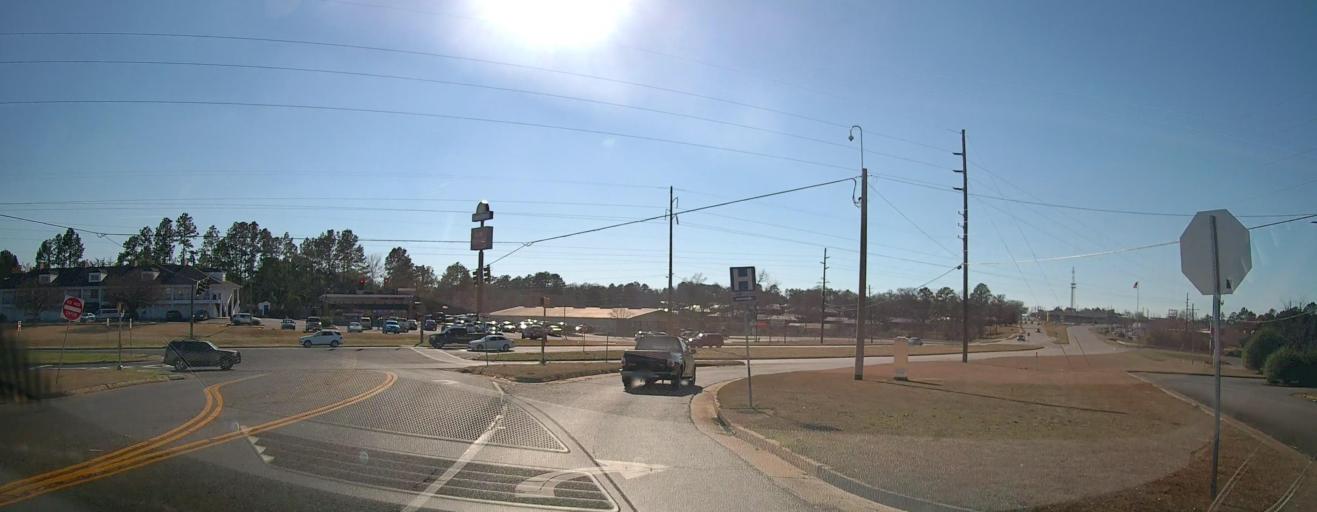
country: US
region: Georgia
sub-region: Sumter County
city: Americus
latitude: 32.0709
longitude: -84.2076
